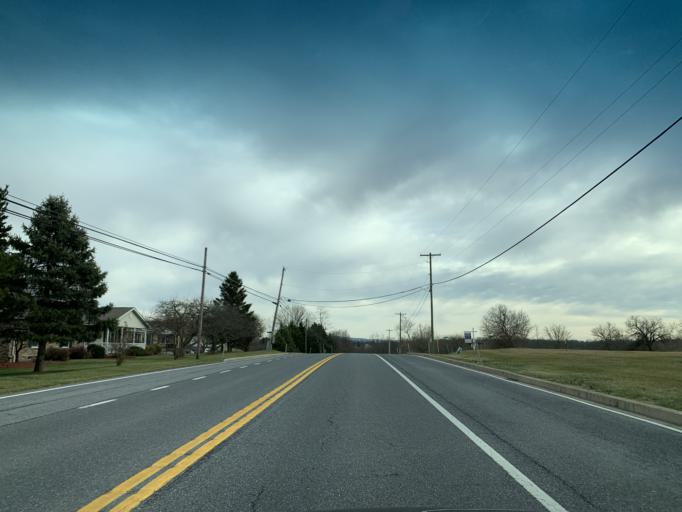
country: US
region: Maryland
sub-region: Washington County
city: Robinwood
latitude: 39.5761
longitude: -77.6920
